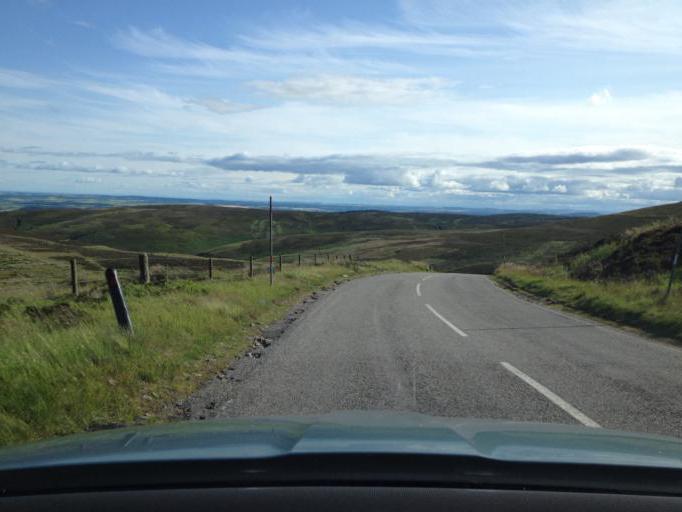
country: GB
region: Scotland
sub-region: Aberdeenshire
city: Laurencekirk
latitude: 56.9126
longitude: -2.5724
